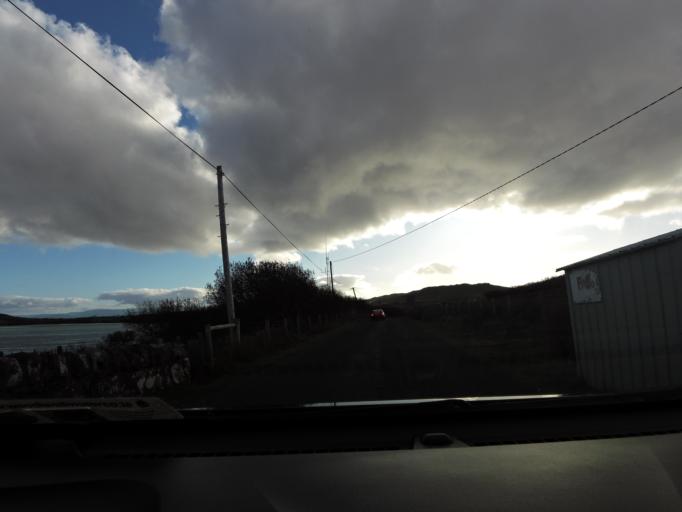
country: IE
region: Connaught
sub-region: Maigh Eo
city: Belmullet
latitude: 53.8834
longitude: -9.9449
